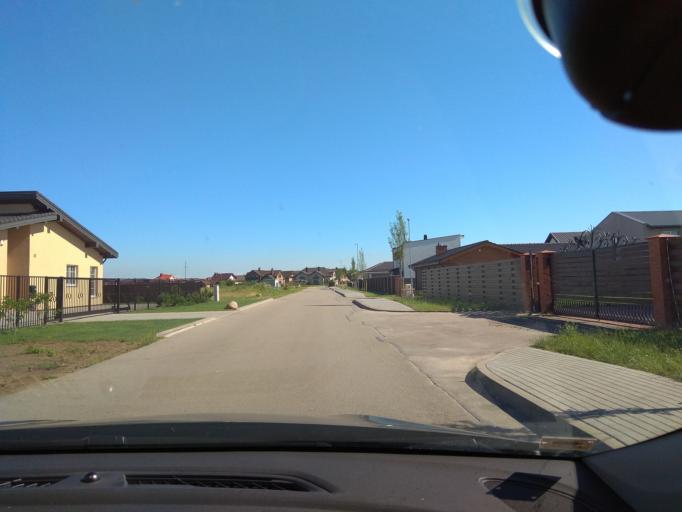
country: LT
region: Klaipedos apskritis
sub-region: Klaipeda
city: Klaipeda
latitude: 55.7508
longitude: 21.1775
